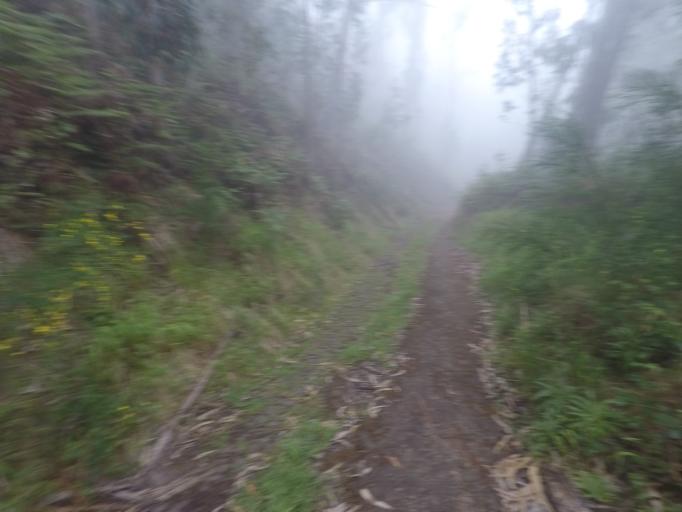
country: PT
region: Madeira
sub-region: Calheta
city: Arco da Calheta
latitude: 32.7260
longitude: -17.0944
